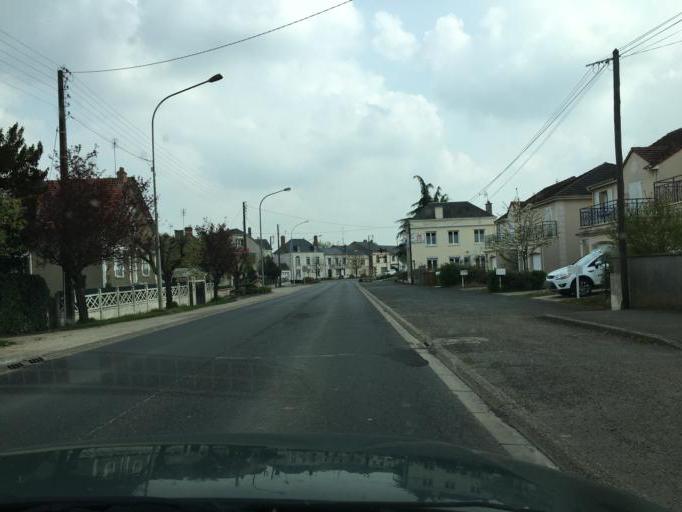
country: FR
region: Centre
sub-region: Departement du Loir-et-Cher
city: Ouzouer-le-Marche
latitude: 47.9114
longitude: 1.5239
